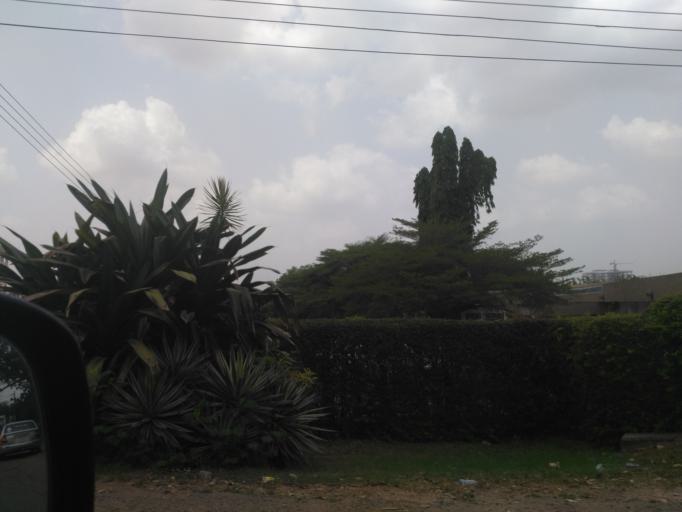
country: GH
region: Greater Accra
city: Accra
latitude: 5.5950
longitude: -0.1821
